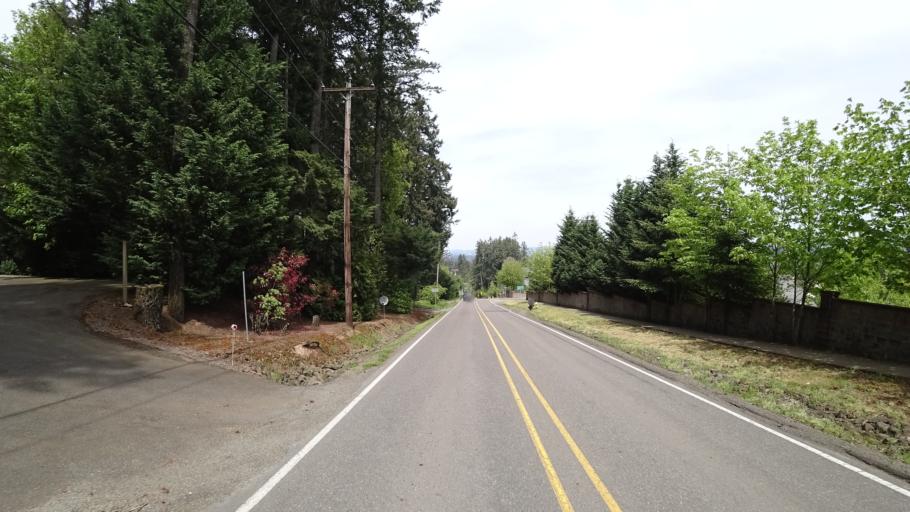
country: US
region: Oregon
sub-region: Washington County
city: Aloha
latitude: 45.4586
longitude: -122.8569
